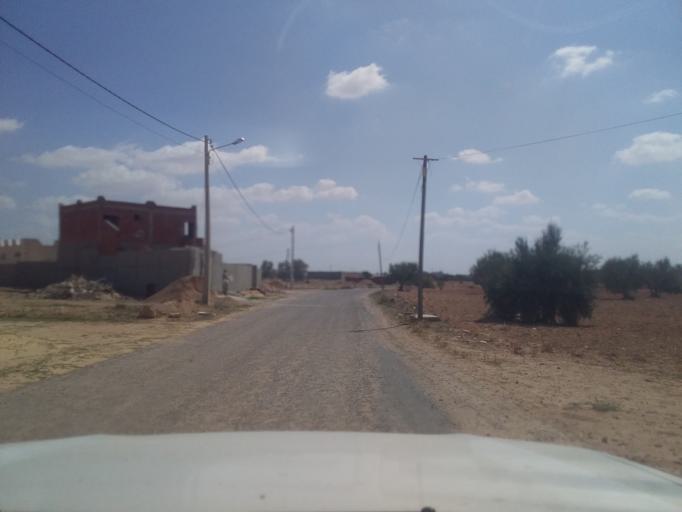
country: TN
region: Madanin
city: Medenine
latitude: 33.6122
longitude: 10.3035
